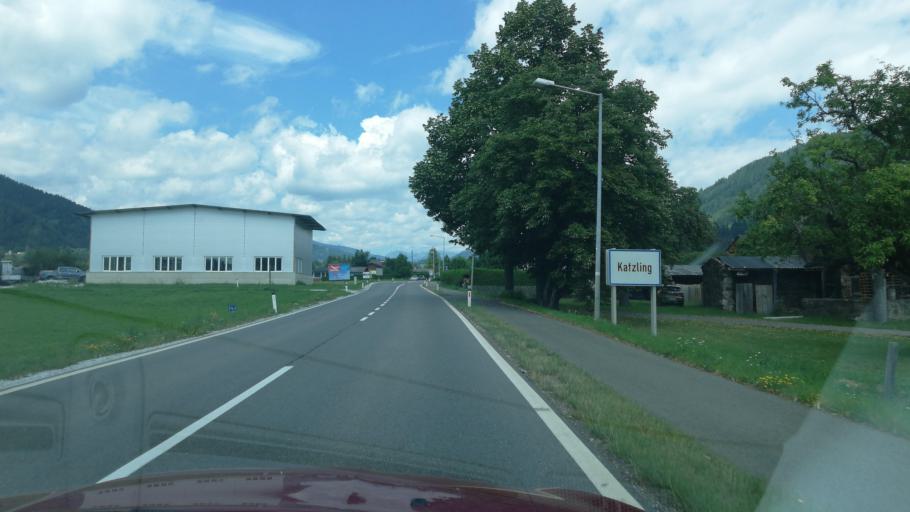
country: AT
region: Styria
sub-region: Politischer Bezirk Murtal
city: Oberkurzheim
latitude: 47.2416
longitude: 14.5347
